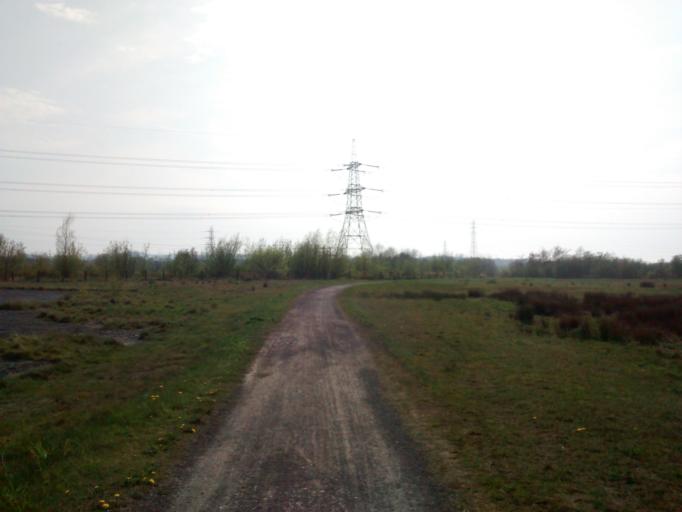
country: GB
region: England
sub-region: County Durham
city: South Hetton
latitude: 54.8048
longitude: -1.3929
